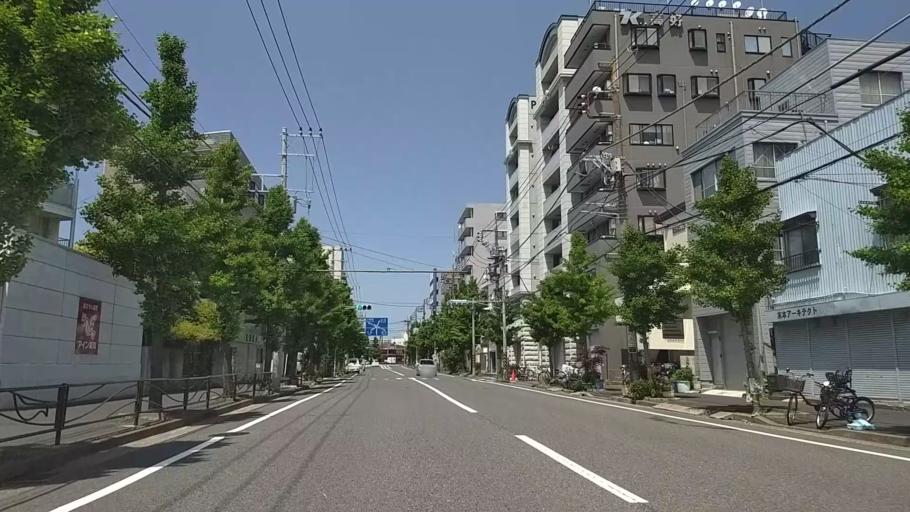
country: JP
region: Kanagawa
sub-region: Kawasaki-shi
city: Kawasaki
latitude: 35.5196
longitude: 139.7133
